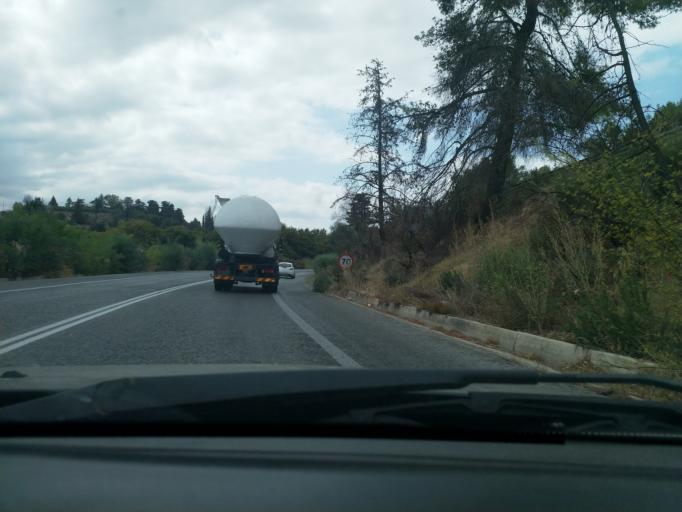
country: GR
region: Crete
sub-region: Nomos Chanias
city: Georgioupolis
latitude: 35.3800
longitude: 24.2007
